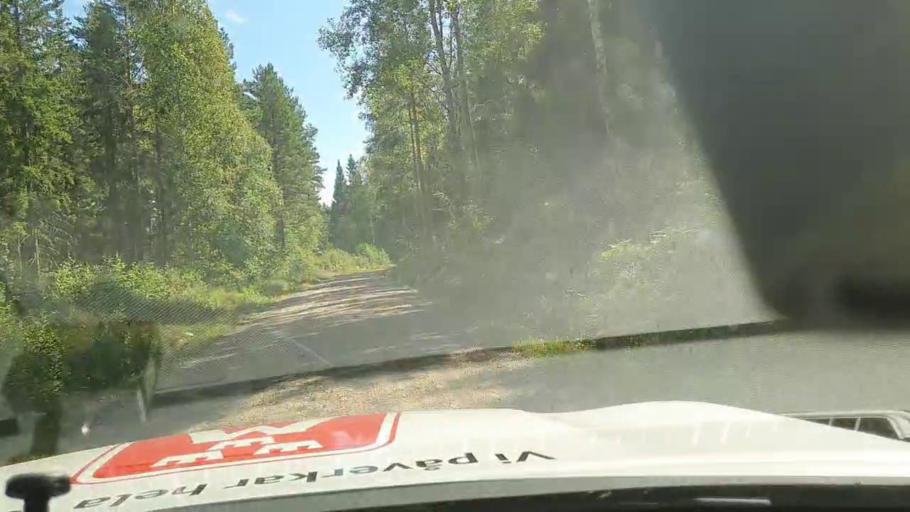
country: SE
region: Soedermanland
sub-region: Strangnas Kommun
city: Akers Styckebruk
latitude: 59.2084
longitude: 16.9173
